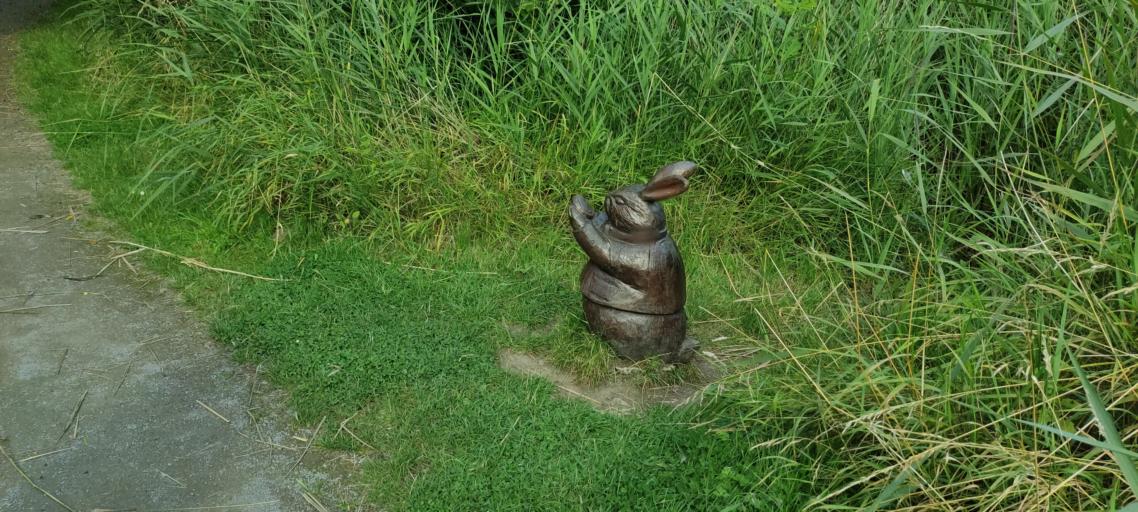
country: GB
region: England
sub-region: Middlesbrough
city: Middlesbrough
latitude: 54.6010
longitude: -1.2245
